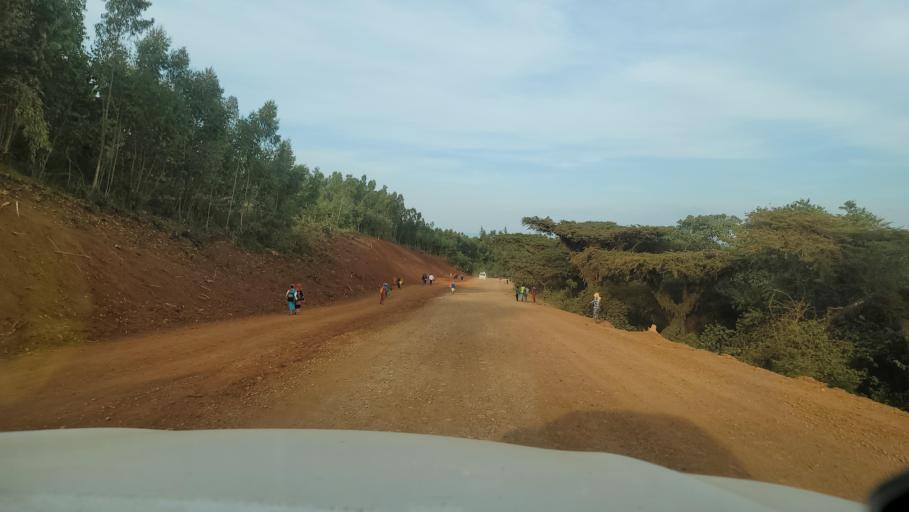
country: ET
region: Oromiya
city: Agaro
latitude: 7.8173
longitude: 36.5244
